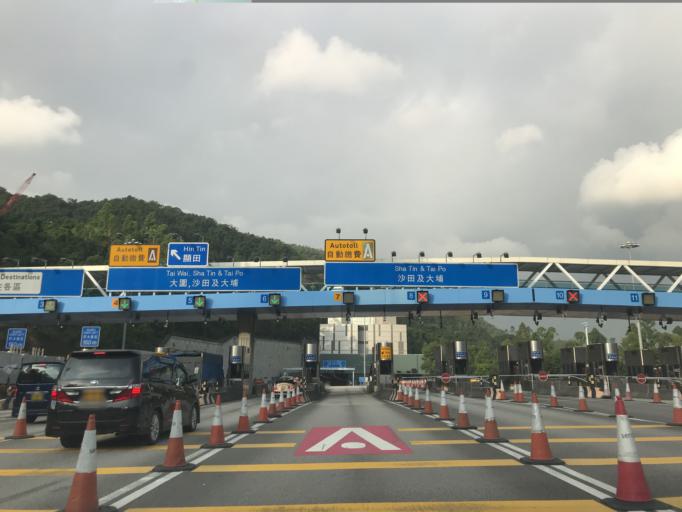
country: HK
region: Wong Tai Sin
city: Wong Tai Sin
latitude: 22.3589
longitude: 114.1629
